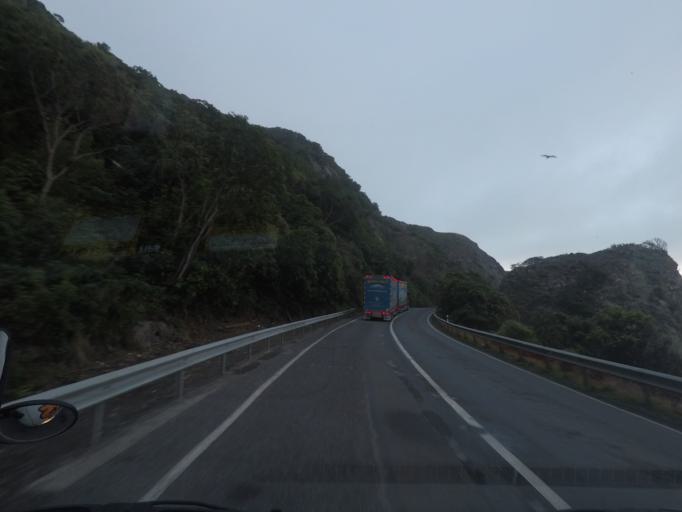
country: NZ
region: Canterbury
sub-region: Kaikoura District
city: Kaikoura
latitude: -42.4498
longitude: 173.5737
